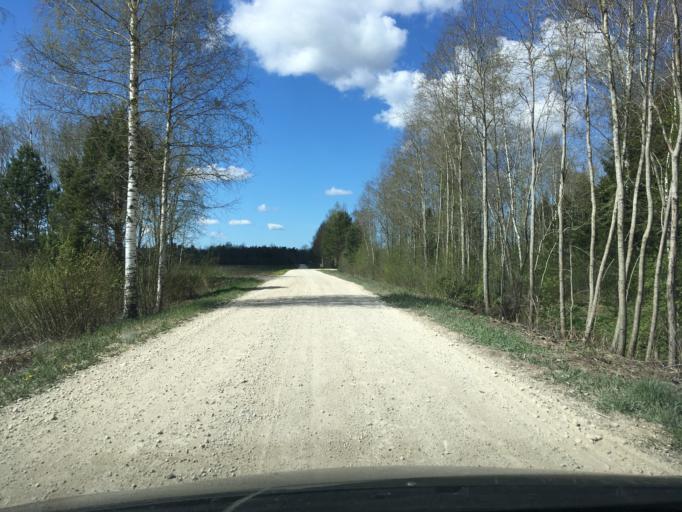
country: EE
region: Harju
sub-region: Raasiku vald
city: Raasiku
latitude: 59.2080
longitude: 25.1747
